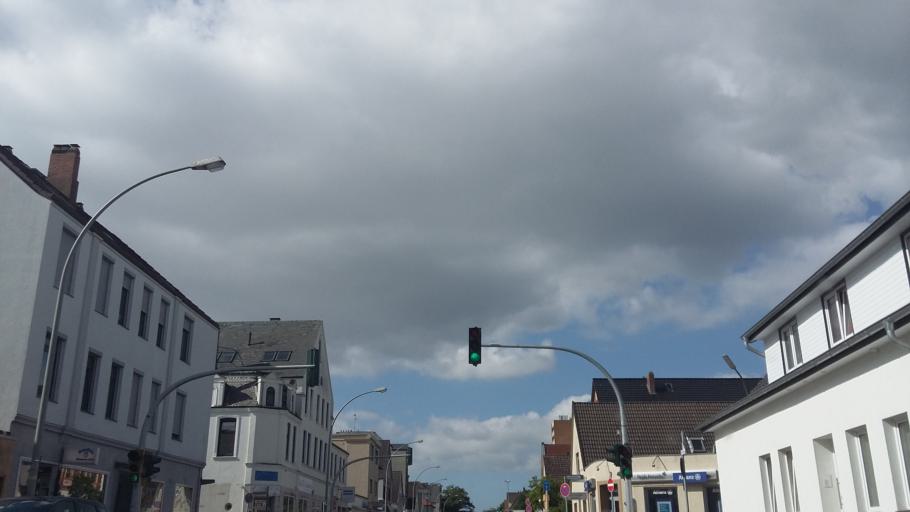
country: DE
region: Bremen
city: Bremerhaven
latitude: 53.5035
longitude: 8.5998
